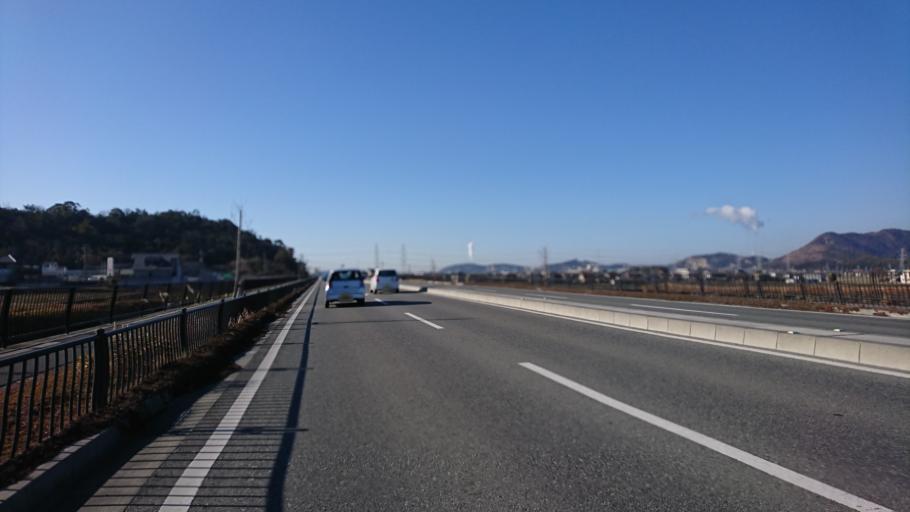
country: JP
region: Hyogo
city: Kakogawacho-honmachi
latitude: 34.8041
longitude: 134.8330
